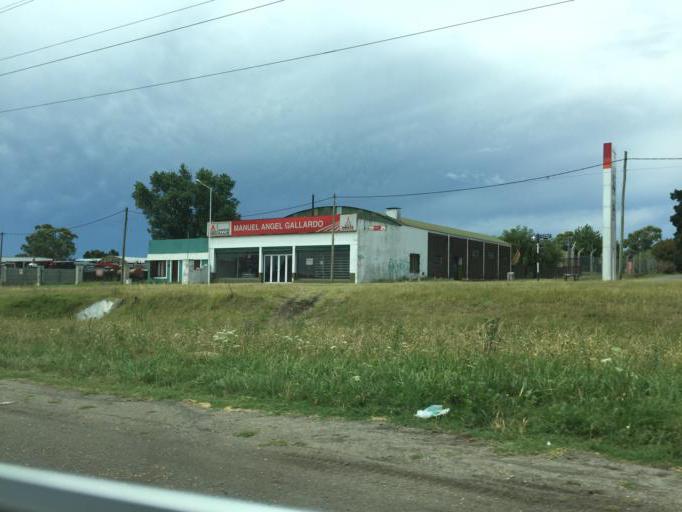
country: AR
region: Buenos Aires
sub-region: Partido de Tandil
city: Tandil
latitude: -37.3182
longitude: -59.1055
